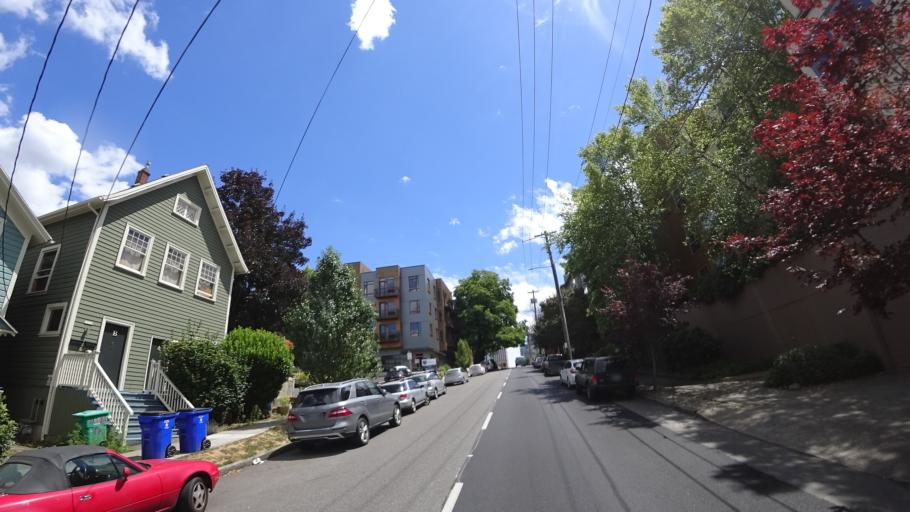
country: US
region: Oregon
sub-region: Multnomah County
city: Portland
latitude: 45.5168
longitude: -122.6902
